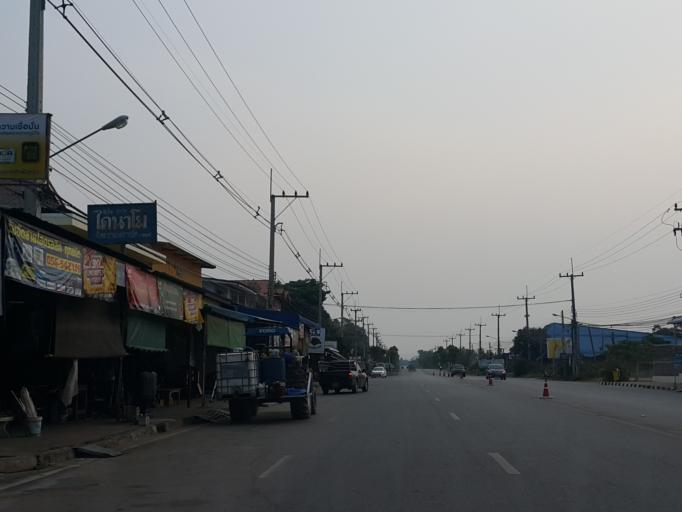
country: TH
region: Uthai Thani
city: Huai Khot
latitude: 15.1751
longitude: 99.6965
